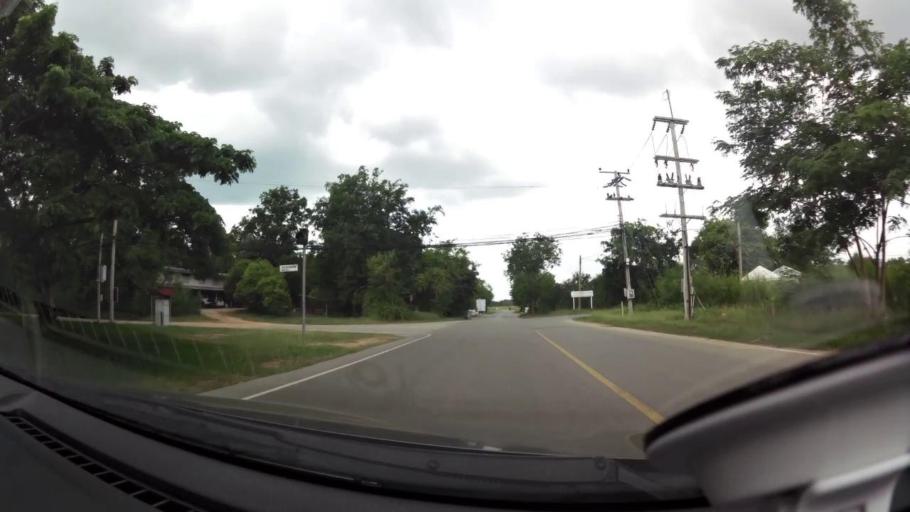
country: TH
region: Phetchaburi
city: Cha-am
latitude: 12.7008
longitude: 99.9583
